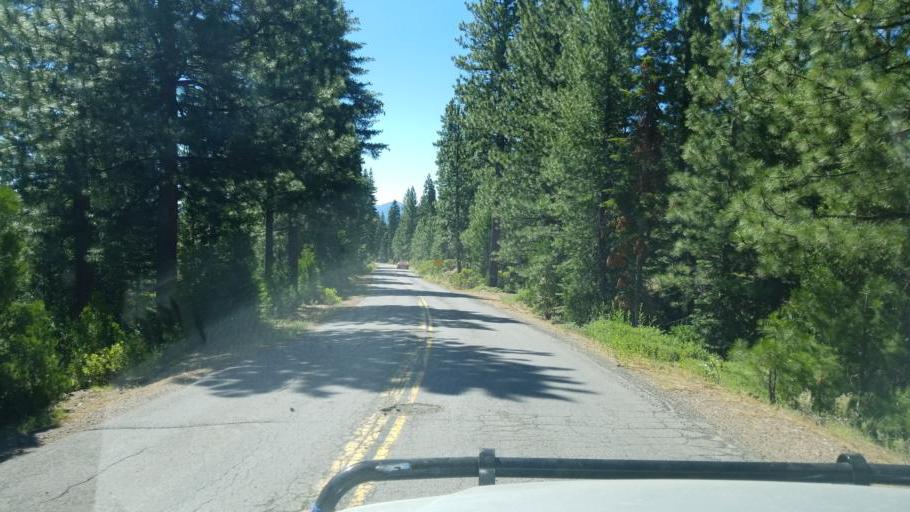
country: US
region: California
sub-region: Lassen County
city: Susanville
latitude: 40.4494
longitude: -120.7617
